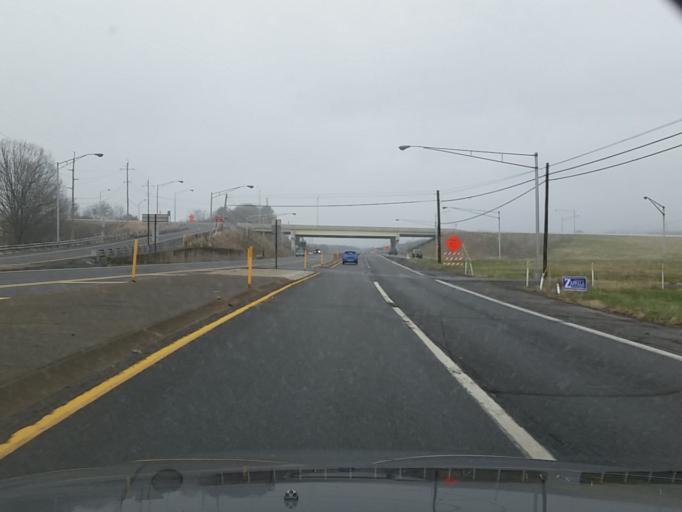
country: US
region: Pennsylvania
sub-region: Luzerne County
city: Nanticoke
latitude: 41.2085
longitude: -75.9845
